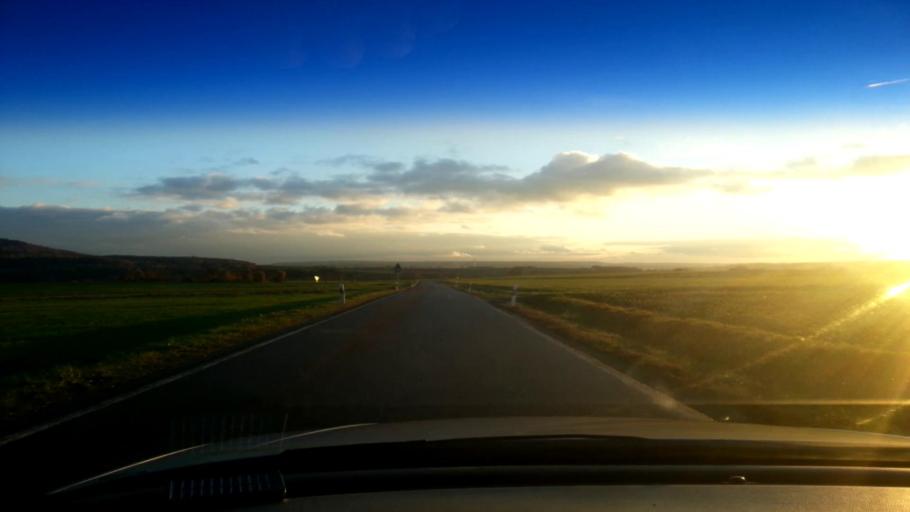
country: DE
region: Bavaria
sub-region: Upper Franconia
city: Buttenheim
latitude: 49.8166
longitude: 11.0536
